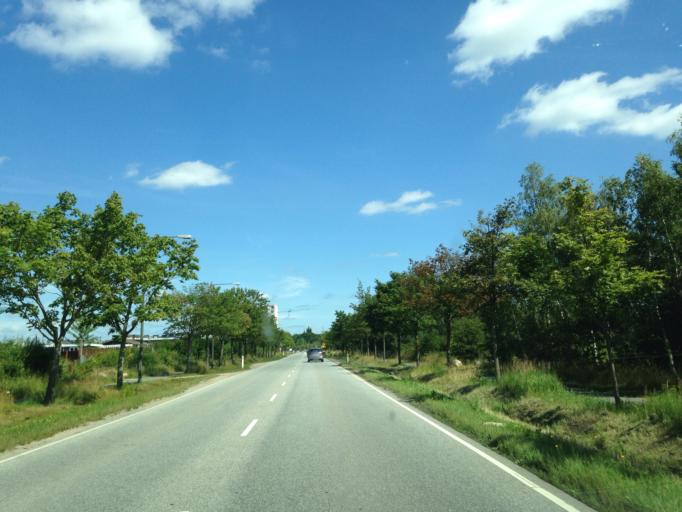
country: DK
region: Capital Region
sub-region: Kobenhavn
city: Copenhagen
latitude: 55.6502
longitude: 12.5665
